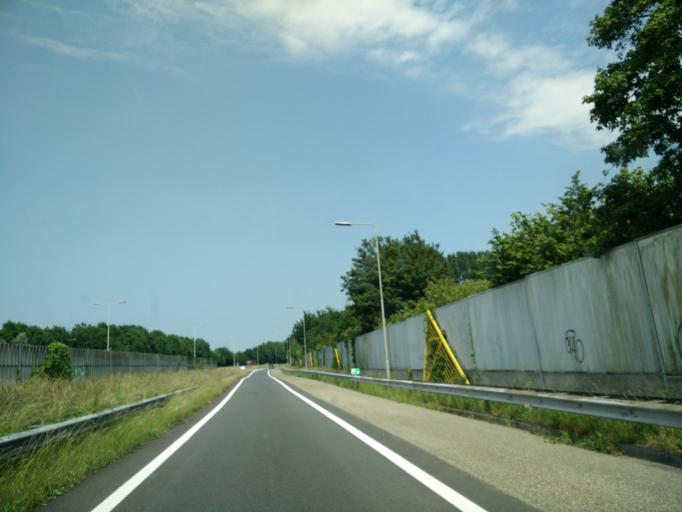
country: NL
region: South Holland
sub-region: Gemeente Dordrecht
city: Dordrecht
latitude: 51.7855
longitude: 4.6691
